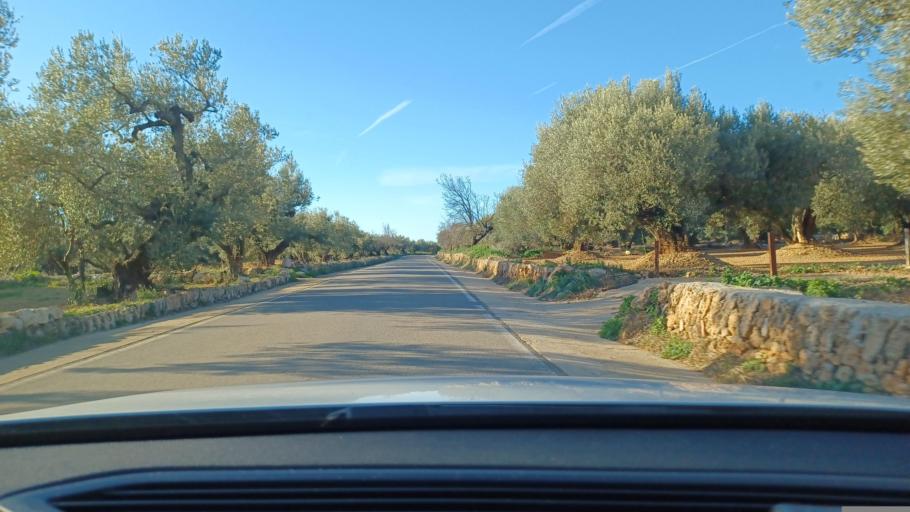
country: ES
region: Catalonia
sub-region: Provincia de Tarragona
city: Mas de Barberans
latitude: 40.7196
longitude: 0.3639
